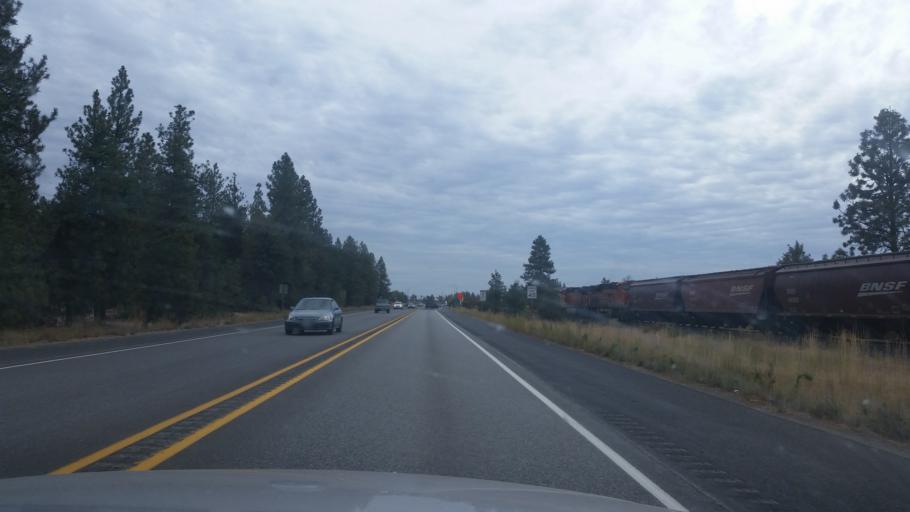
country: US
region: Washington
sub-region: Spokane County
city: Cheney
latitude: 47.5120
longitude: -117.5647
